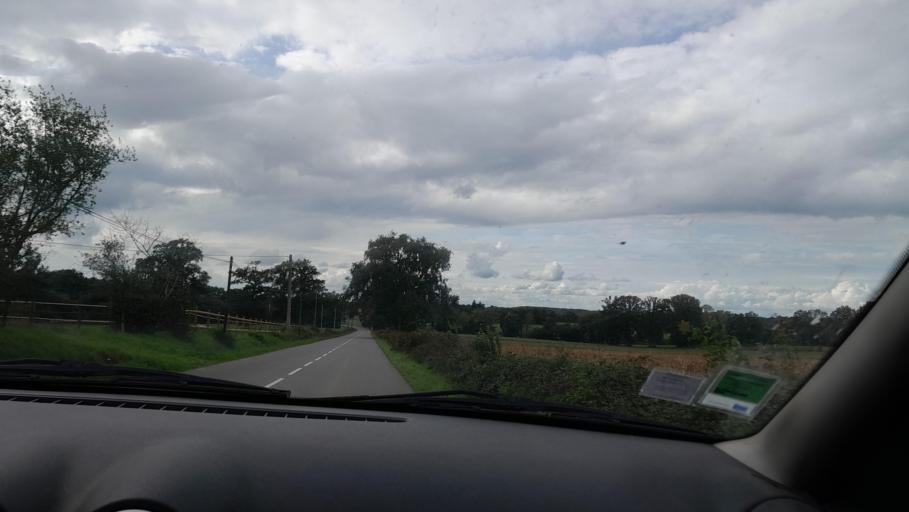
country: FR
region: Brittany
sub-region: Departement d'Ille-et-Vilaine
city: Argentre-du-Plessis
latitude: 48.0524
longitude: -1.1052
